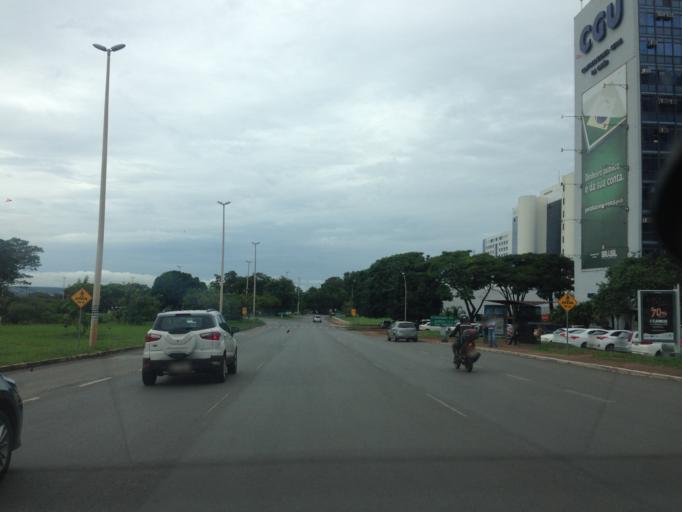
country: BR
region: Federal District
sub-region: Brasilia
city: Brasilia
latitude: -15.8003
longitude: -47.8777
